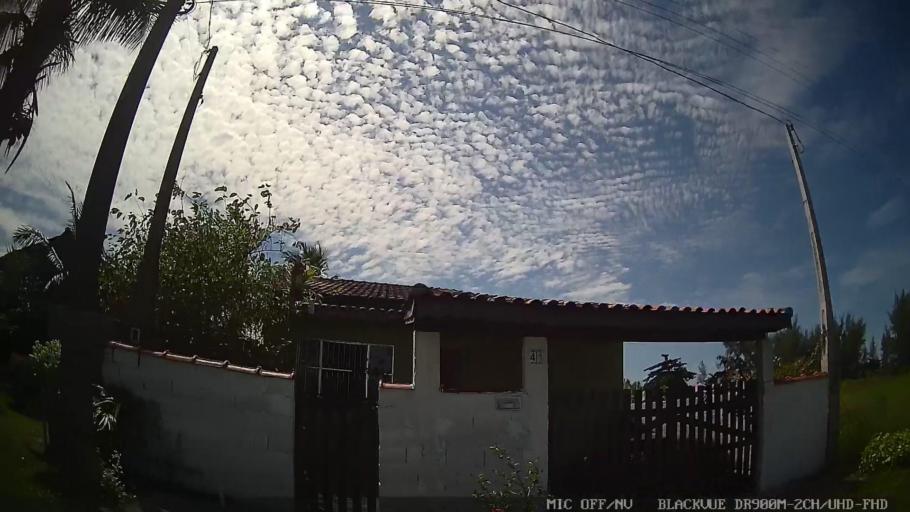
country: BR
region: Sao Paulo
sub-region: Iguape
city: Iguape
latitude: -24.7981
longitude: -47.6285
